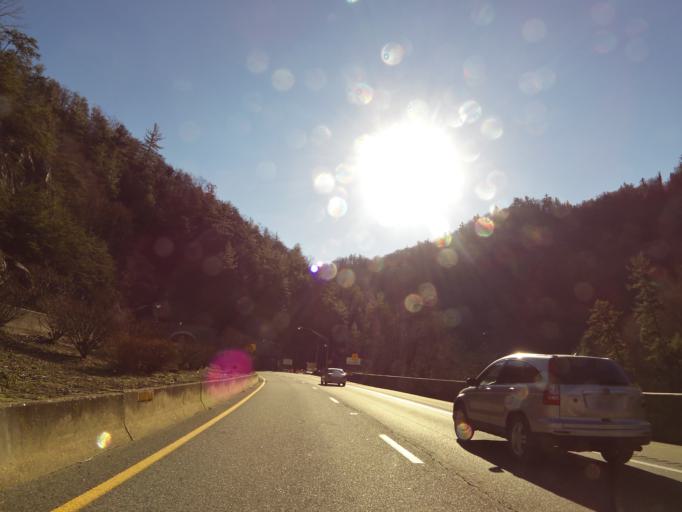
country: US
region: North Carolina
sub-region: Haywood County
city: Cove Creek
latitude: 35.7556
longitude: -83.0480
